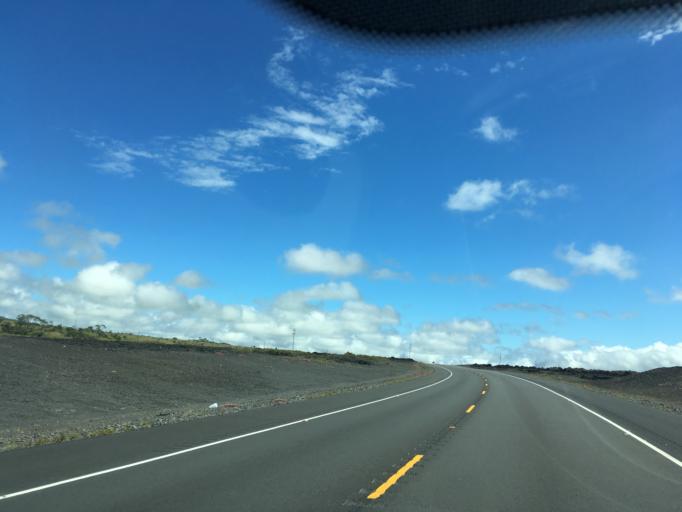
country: US
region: Hawaii
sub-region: Hawaii County
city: Volcano
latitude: 19.6858
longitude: -155.4419
